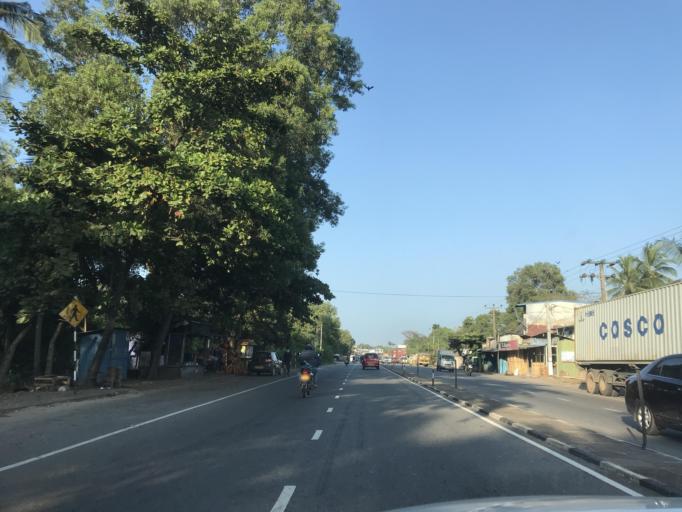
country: LK
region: Western
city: Ja Ela
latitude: 7.0975
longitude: 79.9072
